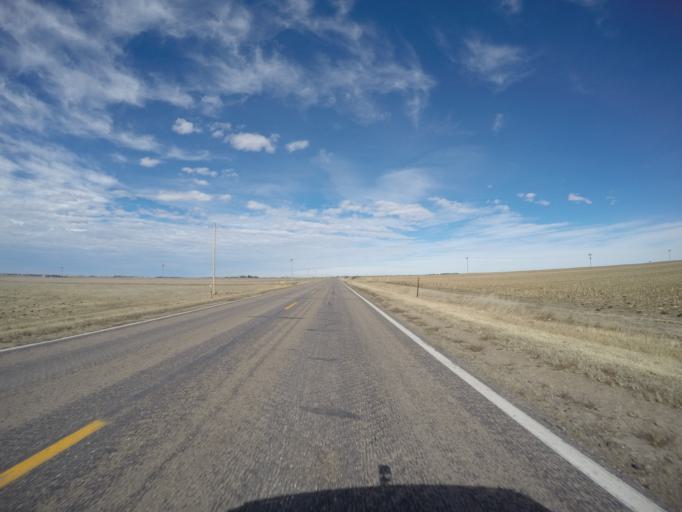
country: US
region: Nebraska
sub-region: Franklin County
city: Franklin
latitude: 40.2332
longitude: -98.9524
